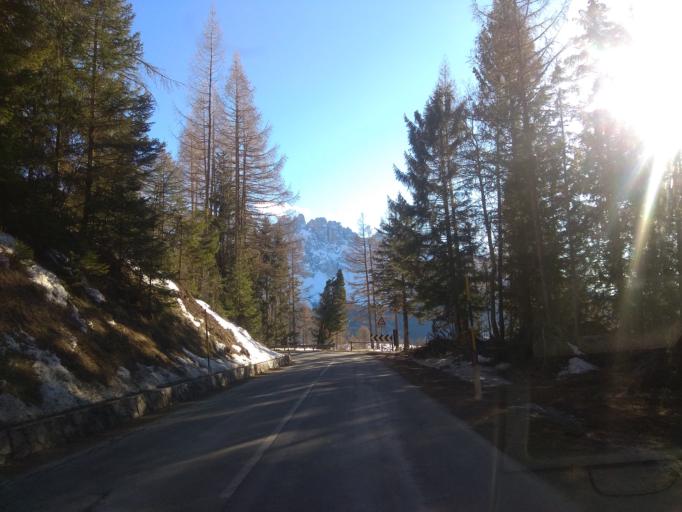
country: IT
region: Trentino-Alto Adige
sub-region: Bolzano
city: Nova Levante
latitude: 46.4247
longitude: 11.5965
